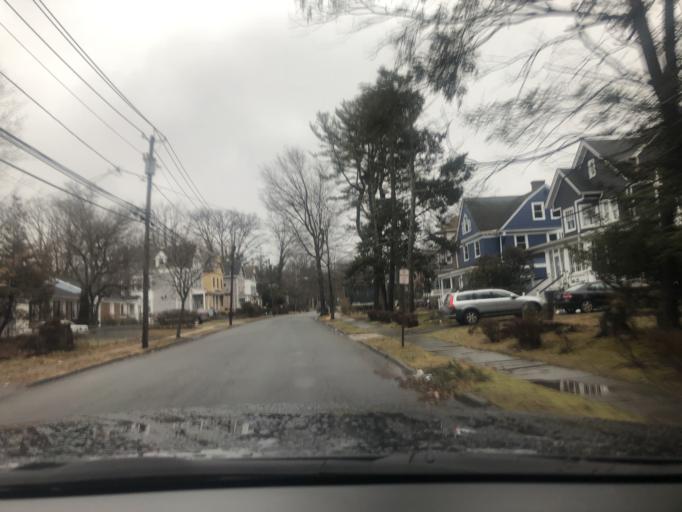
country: US
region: New Jersey
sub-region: Essex County
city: Orange
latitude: 40.7597
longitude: -74.2445
